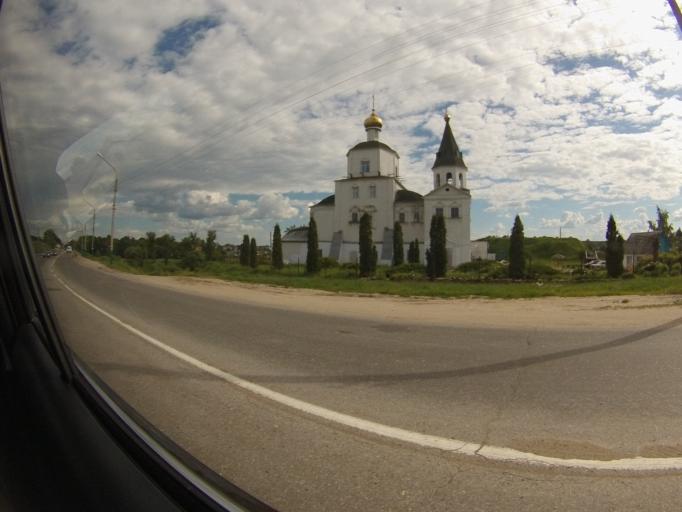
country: RU
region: Orjol
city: Mtsensk
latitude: 53.2841
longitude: 36.5634
